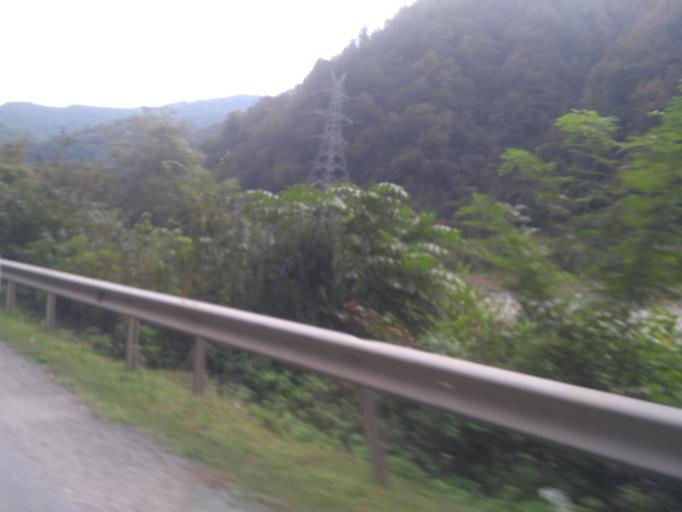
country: TR
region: Artvin
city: Muratli
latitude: 41.5475
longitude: 41.7463
